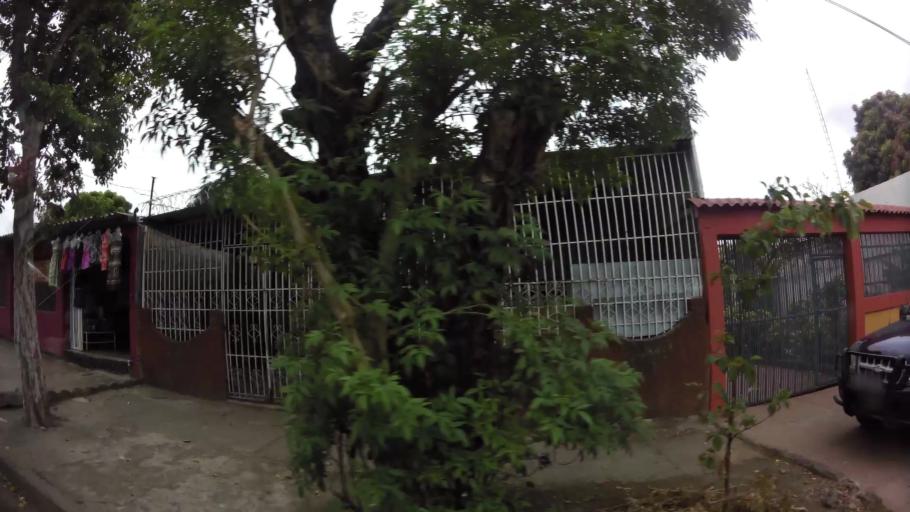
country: NI
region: Managua
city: Managua
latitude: 12.1249
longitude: -86.2394
